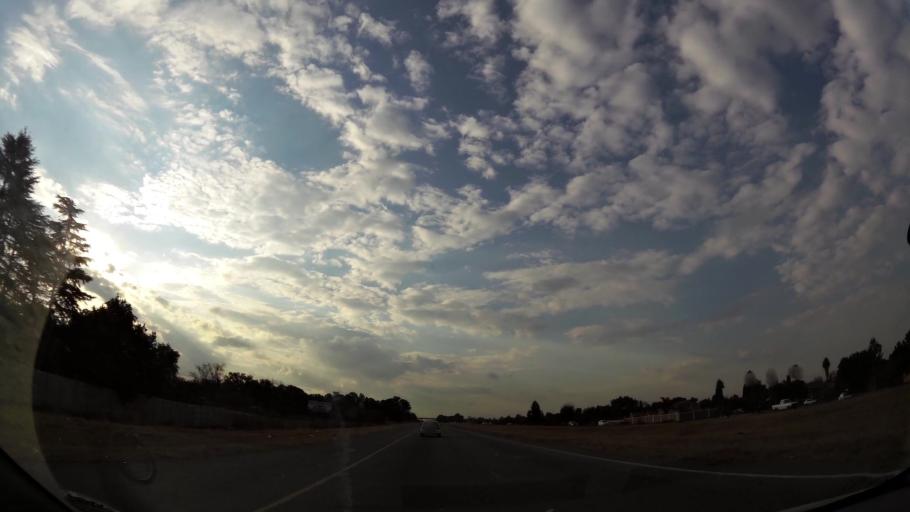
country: ZA
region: Gauteng
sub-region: Sedibeng District Municipality
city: Vanderbijlpark
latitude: -26.7256
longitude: 27.8201
